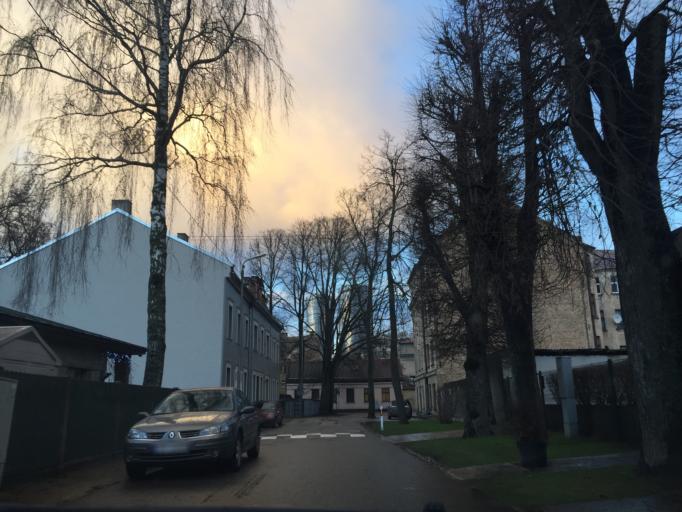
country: LV
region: Riga
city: Riga
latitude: 56.9415
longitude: 24.0777
